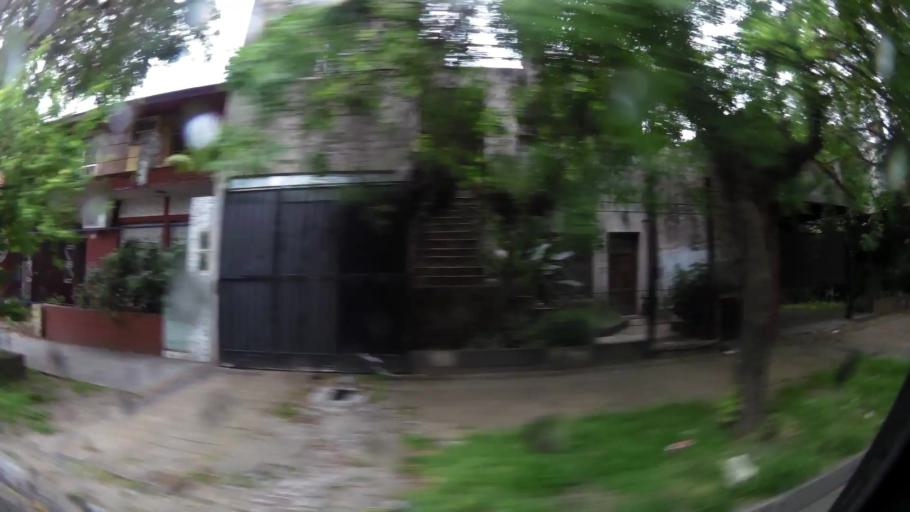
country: AR
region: Buenos Aires
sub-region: Partido de Lanus
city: Lanus
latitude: -34.6987
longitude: -58.3898
